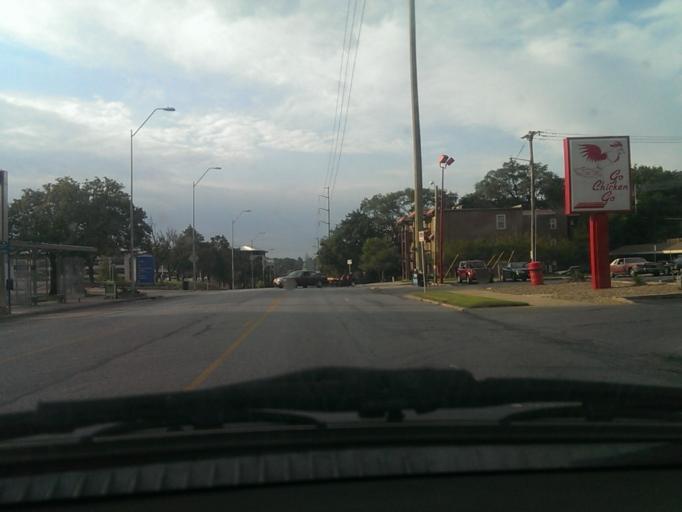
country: US
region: Kansas
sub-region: Johnson County
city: Westwood
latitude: 39.0336
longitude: -94.5733
